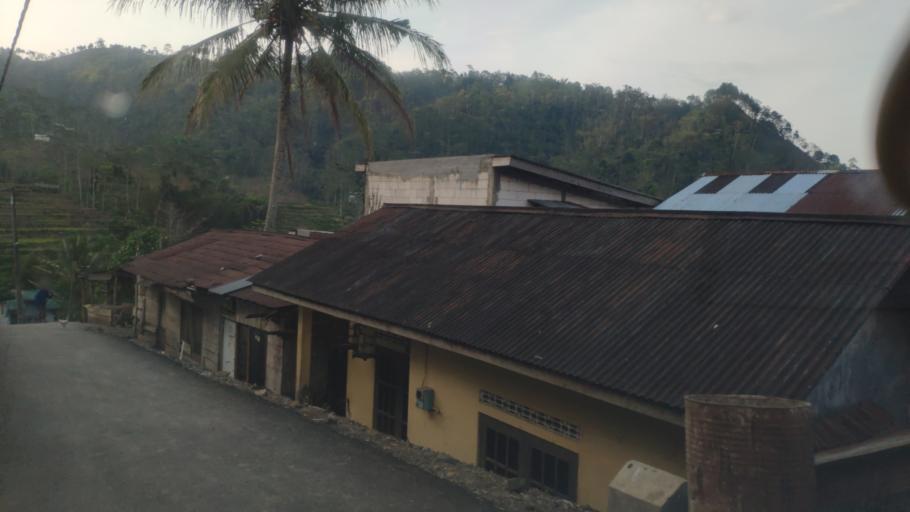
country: ID
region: Central Java
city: Buaran
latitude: -7.2477
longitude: 109.5534
